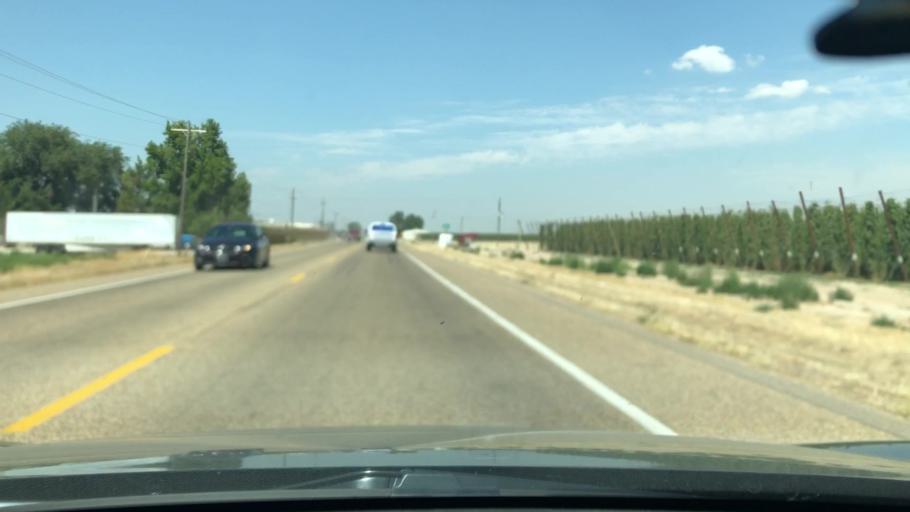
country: US
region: Idaho
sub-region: Canyon County
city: Wilder
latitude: 43.6890
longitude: -116.9120
